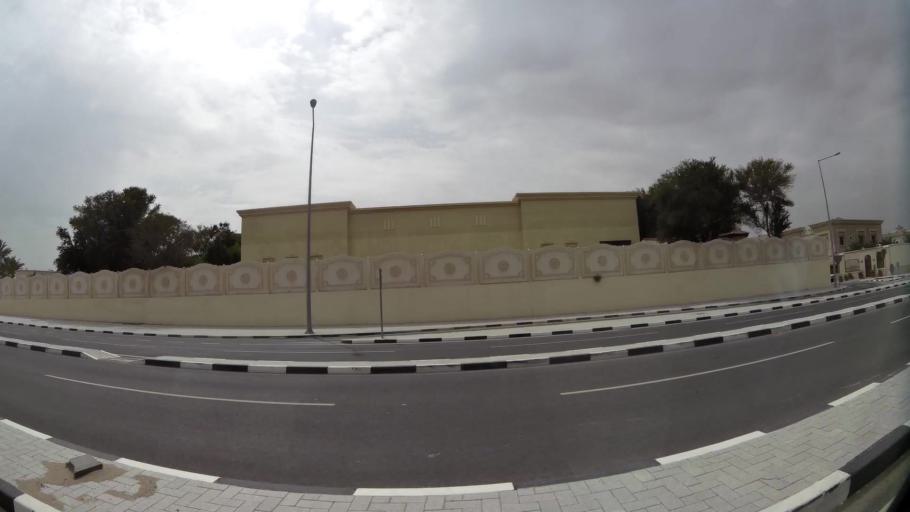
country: QA
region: Baladiyat ar Rayyan
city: Ar Rayyan
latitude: 25.3494
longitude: 51.4669
